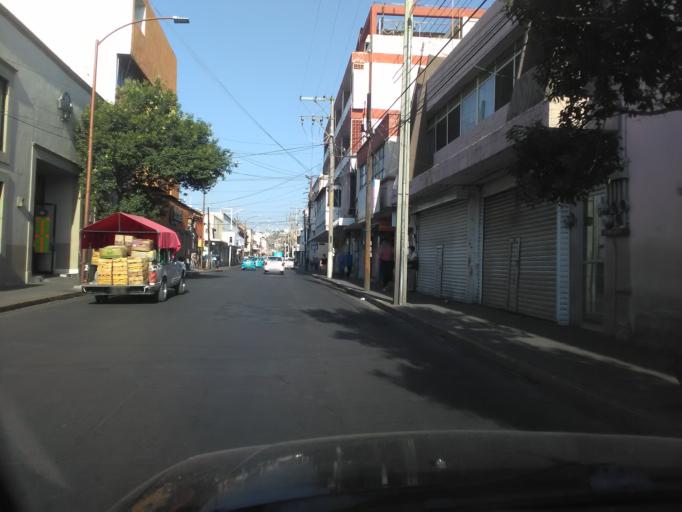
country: MX
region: Durango
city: Victoria de Durango
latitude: 24.0243
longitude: -104.6642
